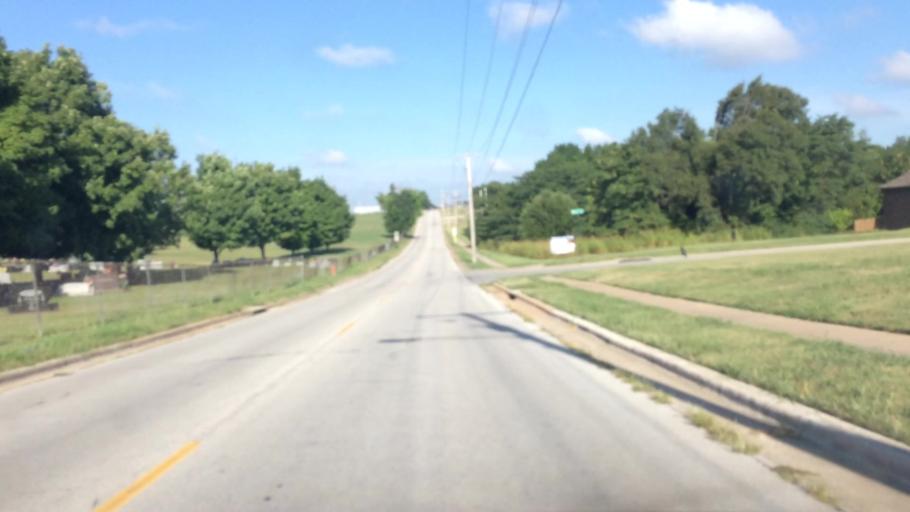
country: US
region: Missouri
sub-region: Greene County
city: Springfield
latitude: 37.2662
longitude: -93.2761
